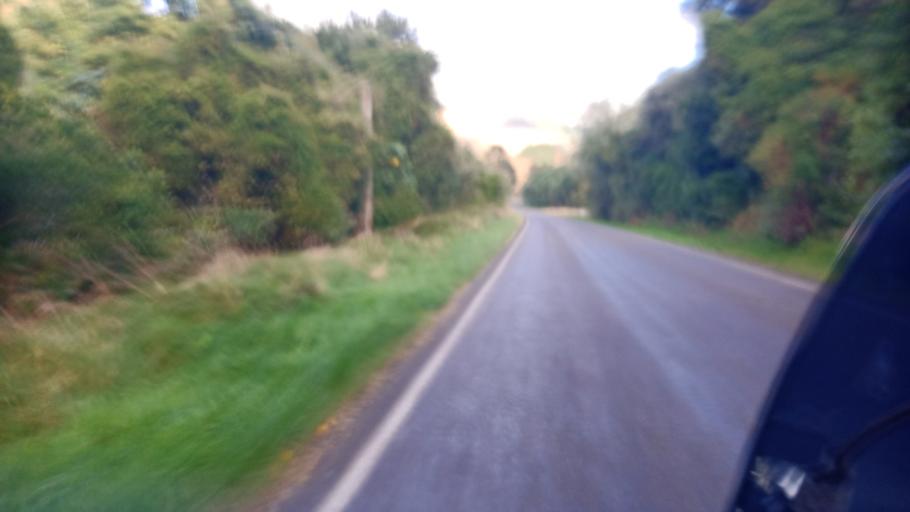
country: NZ
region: Gisborne
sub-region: Gisborne District
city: Gisborne
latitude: -38.5378
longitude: 177.5732
